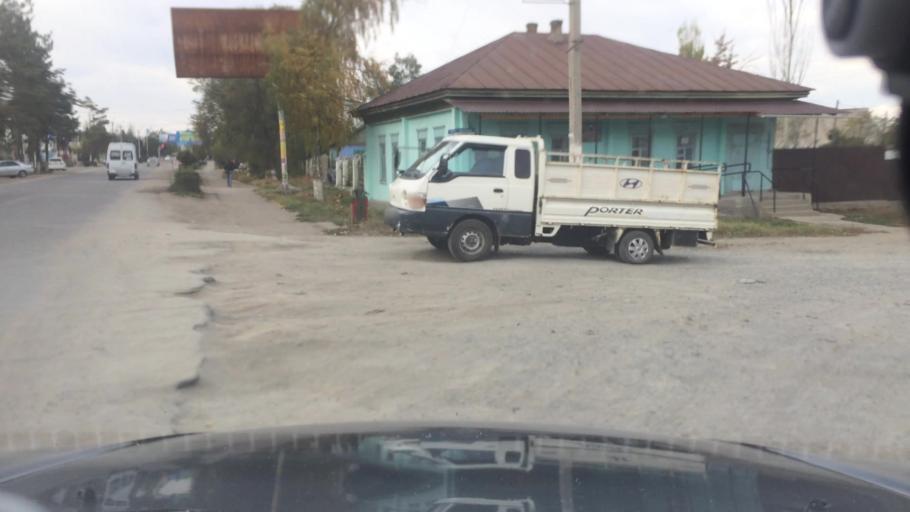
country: KG
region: Ysyk-Koel
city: Karakol
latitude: 42.4890
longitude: 78.3896
